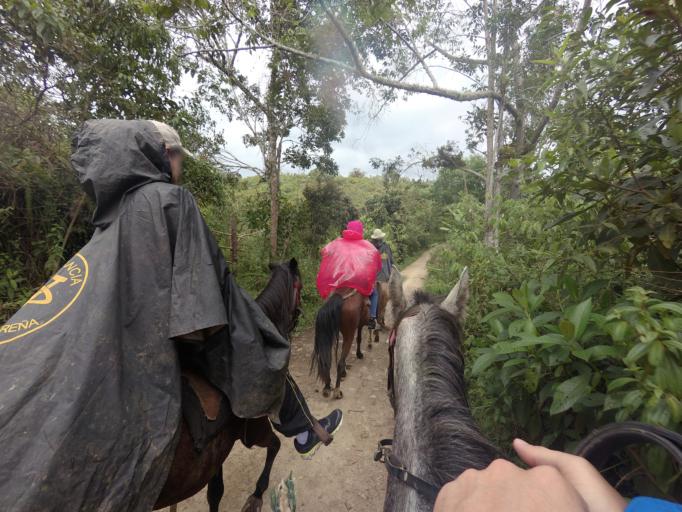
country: CO
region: Huila
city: San Agustin
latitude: 1.9013
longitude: -76.2942
